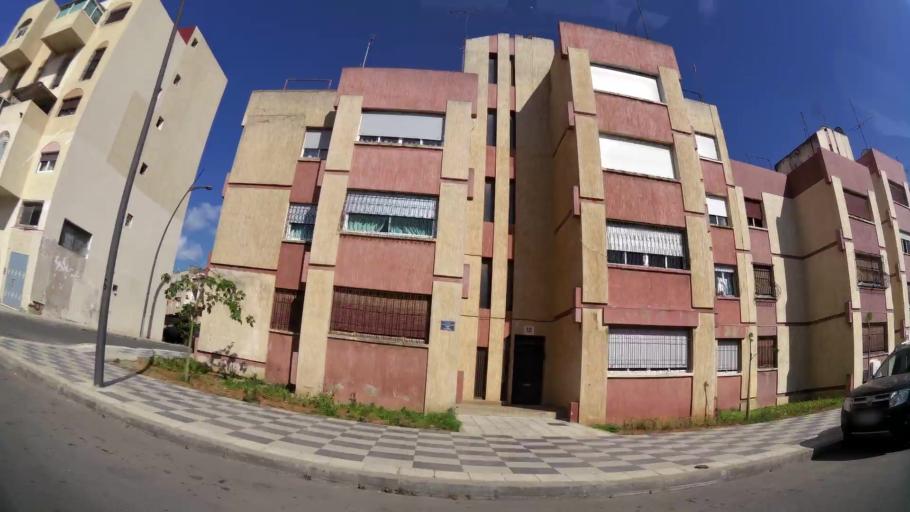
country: MA
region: Rabat-Sale-Zemmour-Zaer
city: Sale
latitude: 34.0452
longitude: -6.7896
